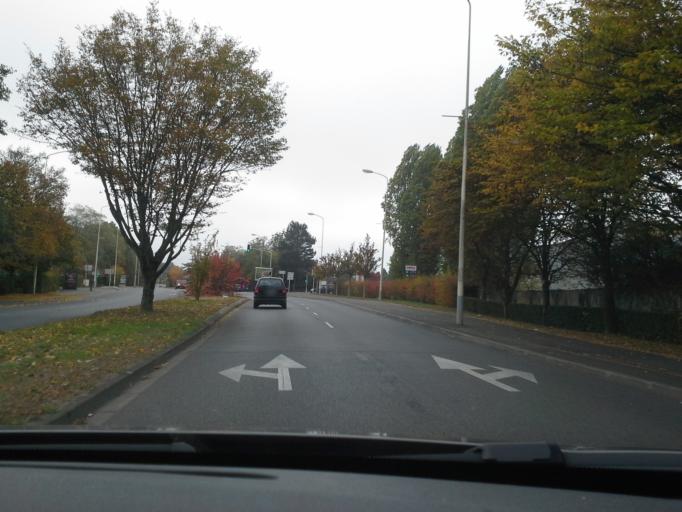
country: FR
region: Centre
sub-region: Departement d'Indre-et-Loire
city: Tours
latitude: 47.4135
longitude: 0.7029
